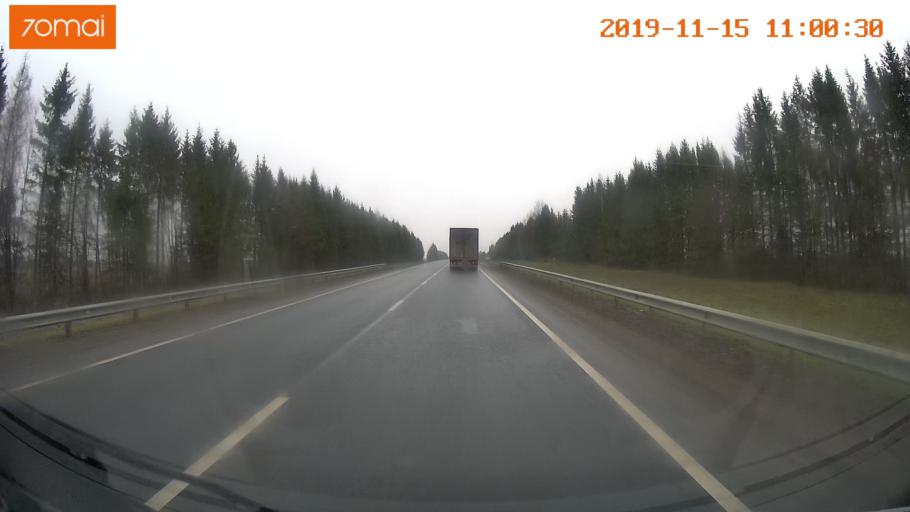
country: RU
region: Vologda
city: Chebsara
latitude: 59.1368
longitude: 38.9011
